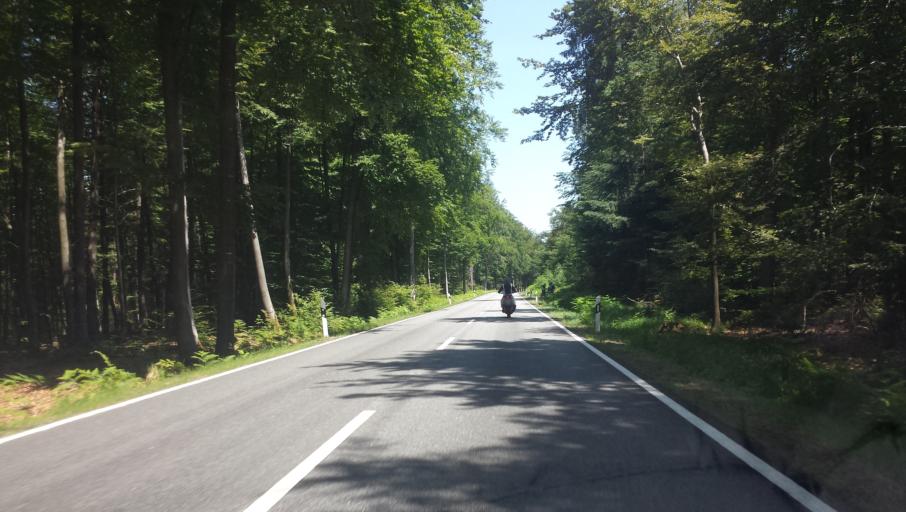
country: DE
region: Rheinland-Pfalz
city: Waldleiningen
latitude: 49.3601
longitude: 7.8393
